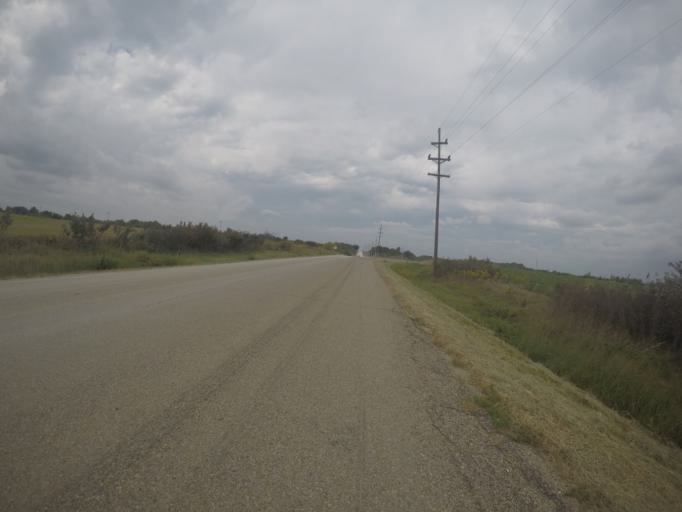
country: US
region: Kansas
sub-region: Morris County
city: Council Grove
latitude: 38.8846
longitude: -96.5558
